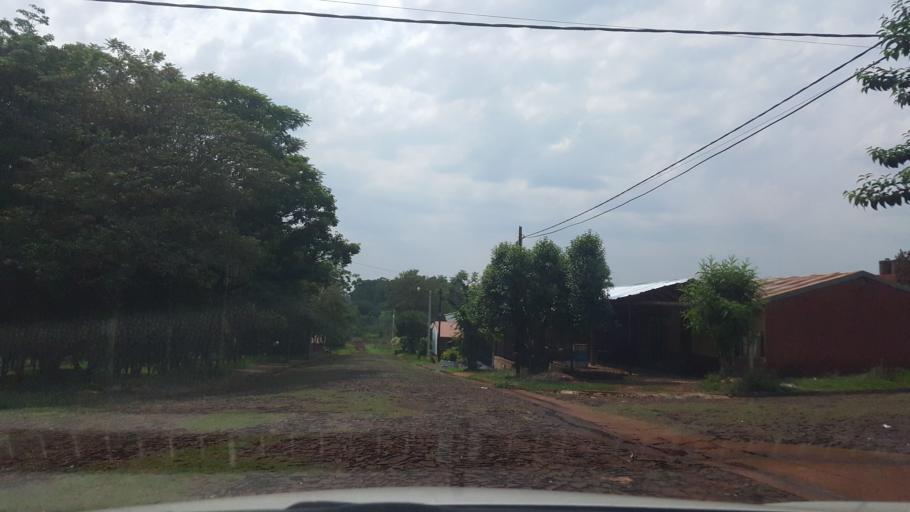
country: AR
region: Misiones
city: Capiovi
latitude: -26.9322
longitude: -55.0547
